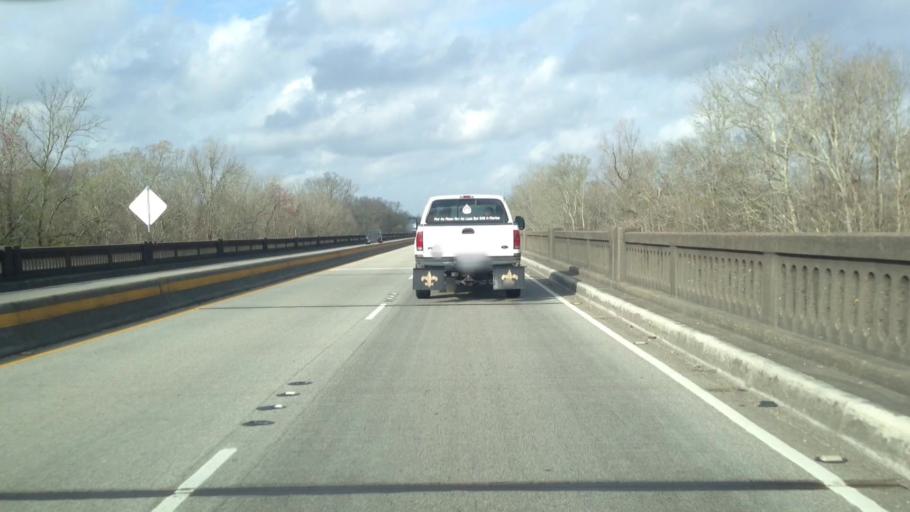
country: US
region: Louisiana
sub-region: Saint Landry Parish
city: Krotz Springs
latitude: 30.5550
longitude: -91.6839
